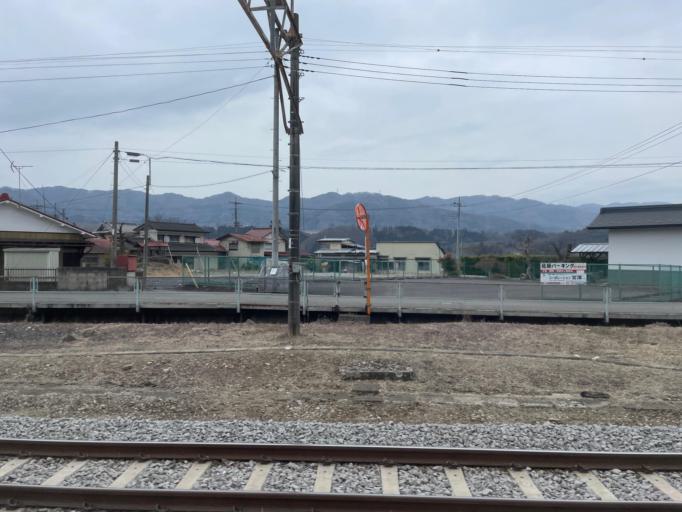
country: JP
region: Gunma
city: Numata
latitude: 36.6810
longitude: 138.9981
